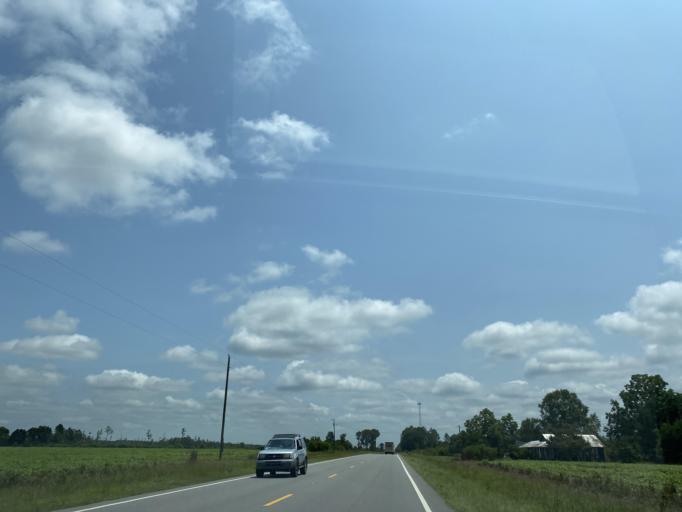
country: US
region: Georgia
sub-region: Jeff Davis County
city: Hazlehurst
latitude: 31.7355
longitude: -82.5358
